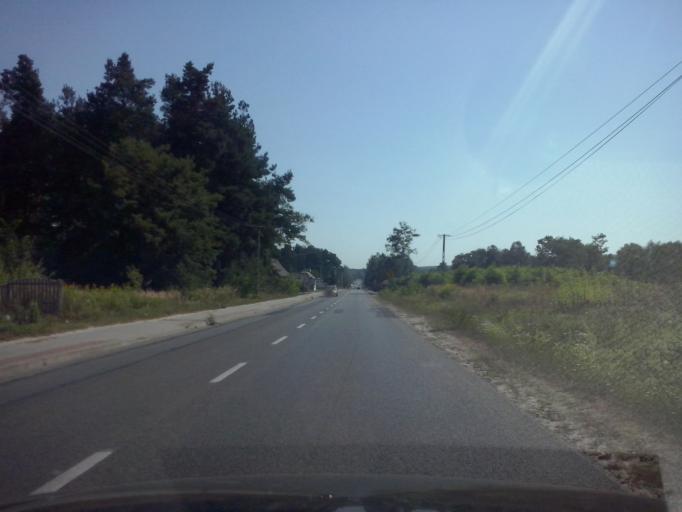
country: PL
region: Swietokrzyskie
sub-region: Powiat kielecki
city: Domaszowice
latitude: 50.8141
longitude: 20.6927
